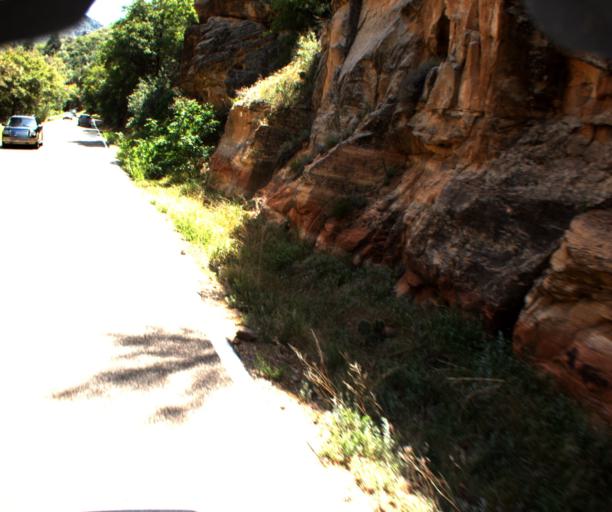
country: US
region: Arizona
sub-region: Coconino County
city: Sedona
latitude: 34.9221
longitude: -111.7348
